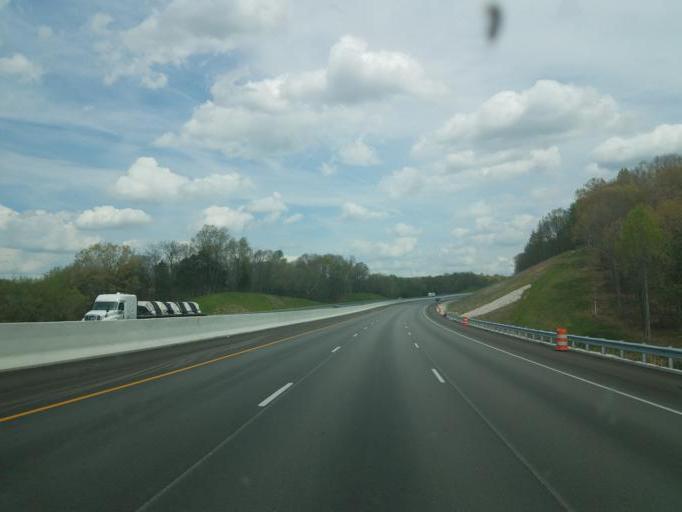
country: US
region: Kentucky
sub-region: Hart County
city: Munfordville
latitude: 37.3343
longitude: -85.9074
